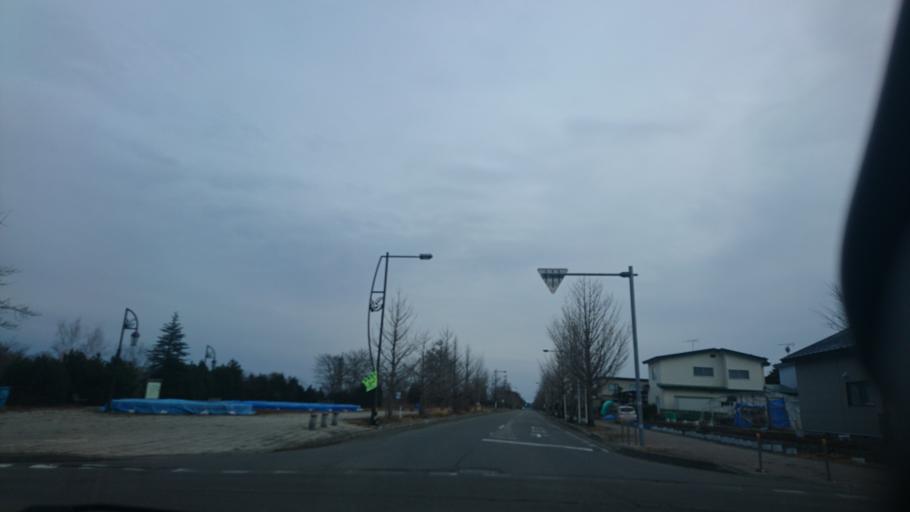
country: JP
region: Hokkaido
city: Otofuke
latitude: 42.9719
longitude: 143.1988
